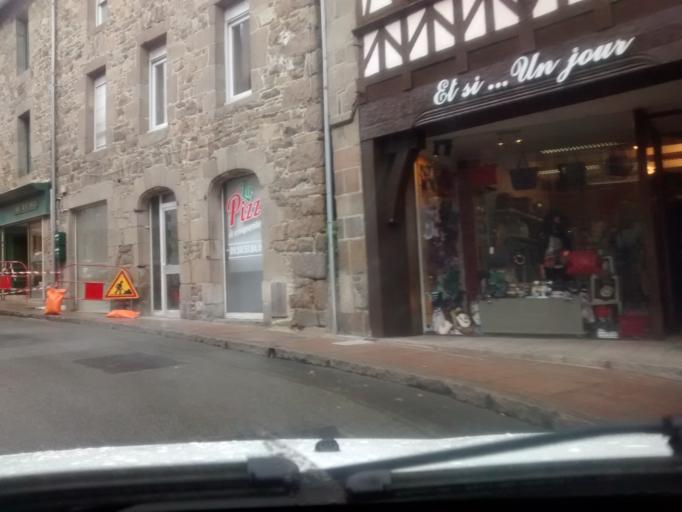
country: FR
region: Brittany
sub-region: Departement des Cotes-d'Armor
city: Treguier
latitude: 48.7870
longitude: -3.2315
